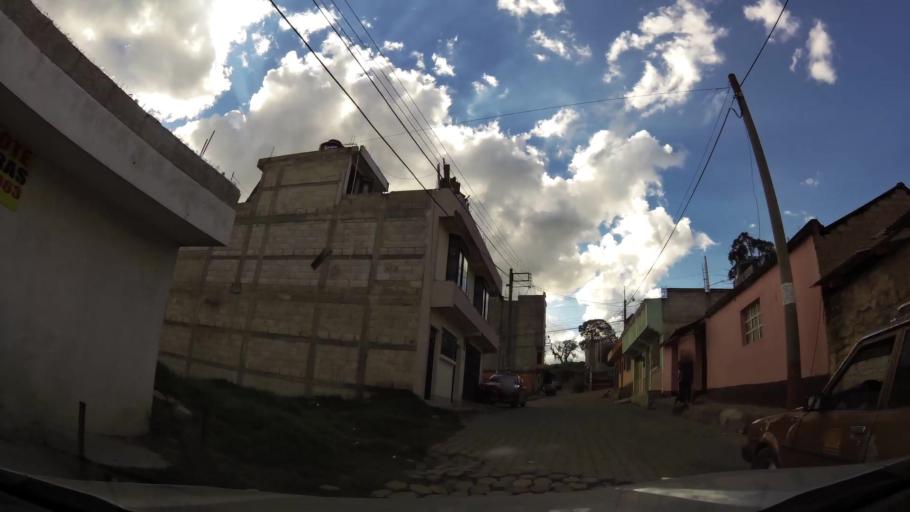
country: GT
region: Quetzaltenango
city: Quetzaltenango
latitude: 14.8526
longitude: -91.5179
